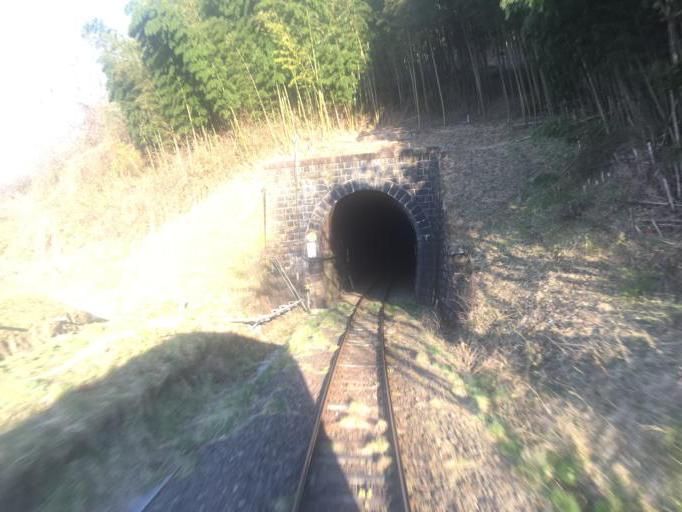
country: JP
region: Fukushima
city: Funehikimachi-funehiki
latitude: 37.4647
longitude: 140.5291
